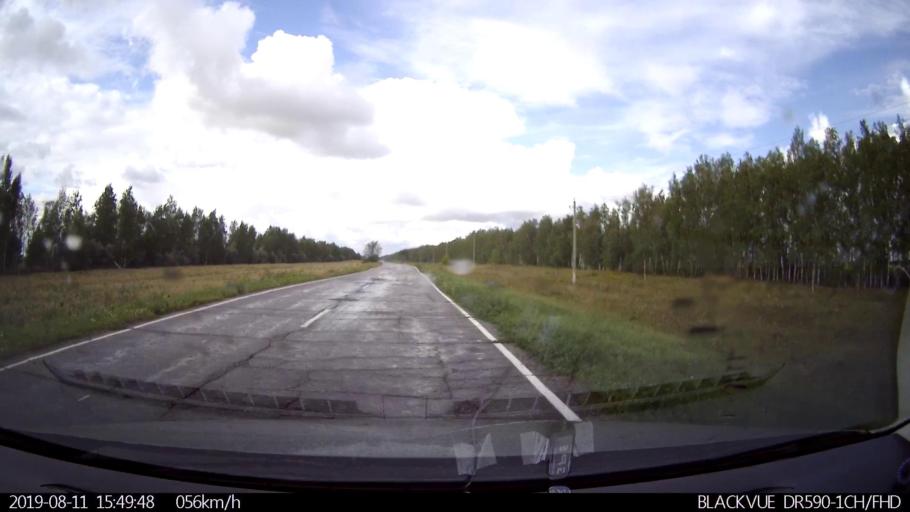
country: RU
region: Ulyanovsk
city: Ignatovka
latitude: 53.9072
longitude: 47.6555
